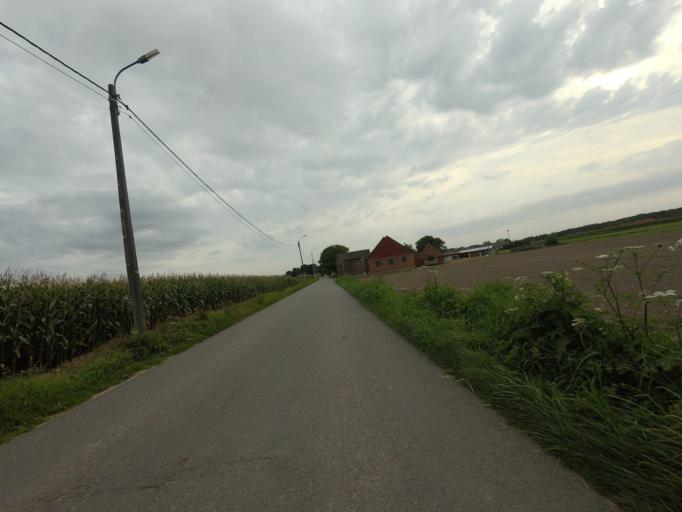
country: BE
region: Flanders
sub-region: Provincie Vlaams-Brabant
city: Grimbergen
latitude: 50.9695
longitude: 4.3545
